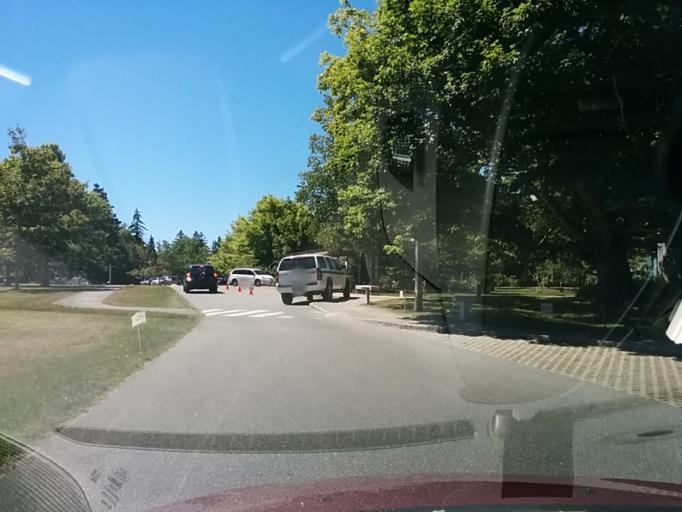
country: US
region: Maine
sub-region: Hancock County
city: Bar Harbor
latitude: 44.3206
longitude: -68.2531
